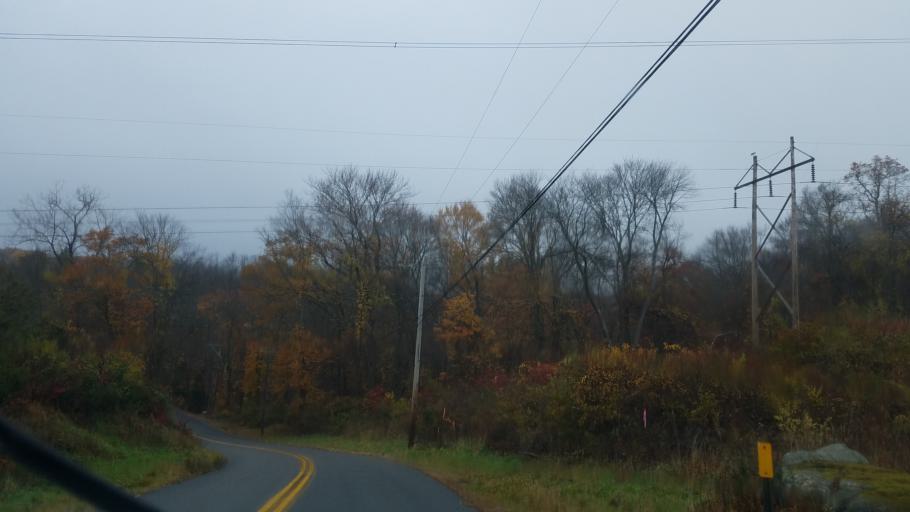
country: US
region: Connecticut
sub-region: Middlesex County
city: Higganum
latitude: 41.5165
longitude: -72.5282
